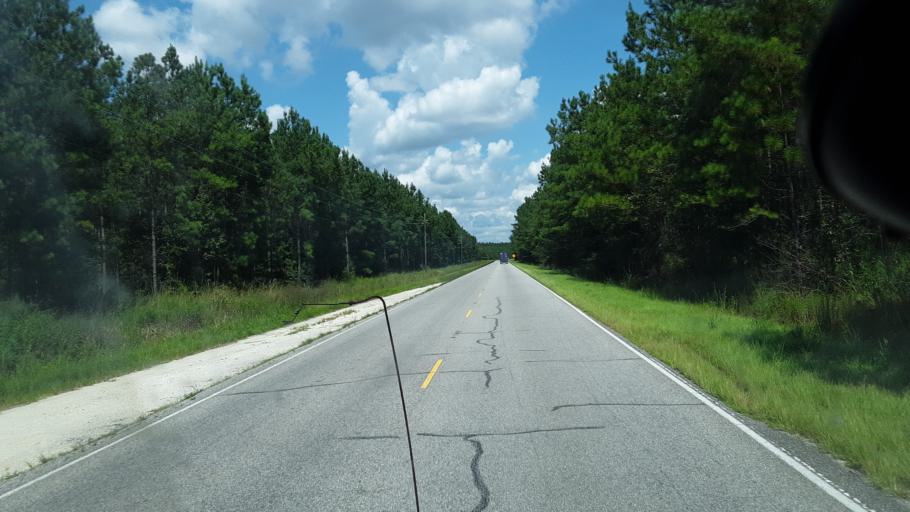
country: US
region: South Carolina
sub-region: Williamsburg County
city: Andrews
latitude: 33.4136
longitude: -79.6058
